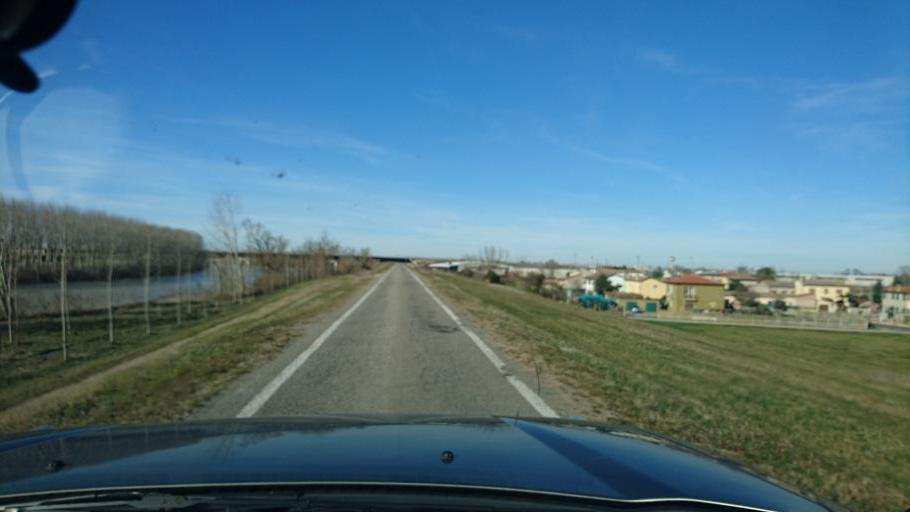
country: IT
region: Veneto
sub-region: Provincia di Rovigo
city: Ariano
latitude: 44.9377
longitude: 12.1292
